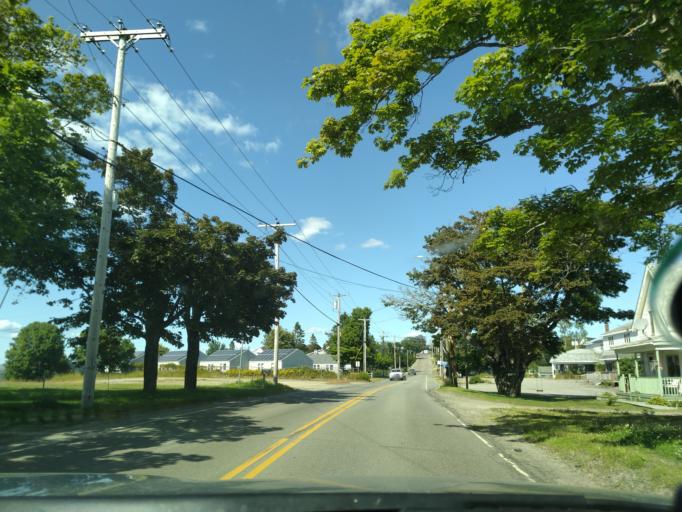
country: US
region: Maine
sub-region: Washington County
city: Eastport
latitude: 44.8563
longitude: -66.9921
